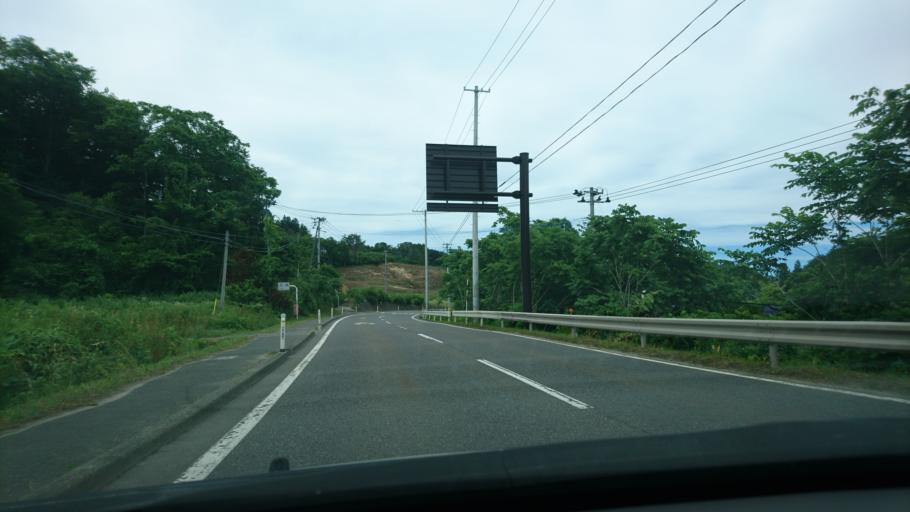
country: JP
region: Iwate
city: Miyako
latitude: 39.9405
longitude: 141.8407
